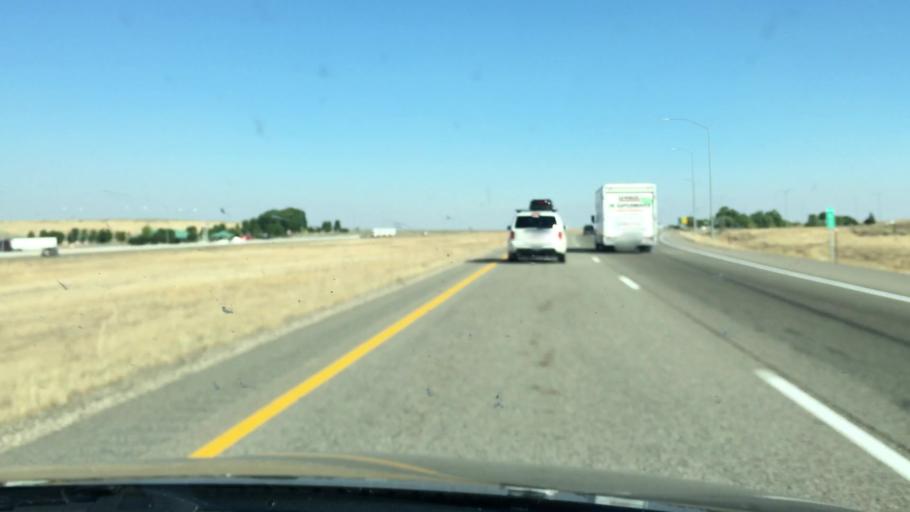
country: US
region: Idaho
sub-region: Ada County
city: Boise
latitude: 43.4807
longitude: -116.1109
